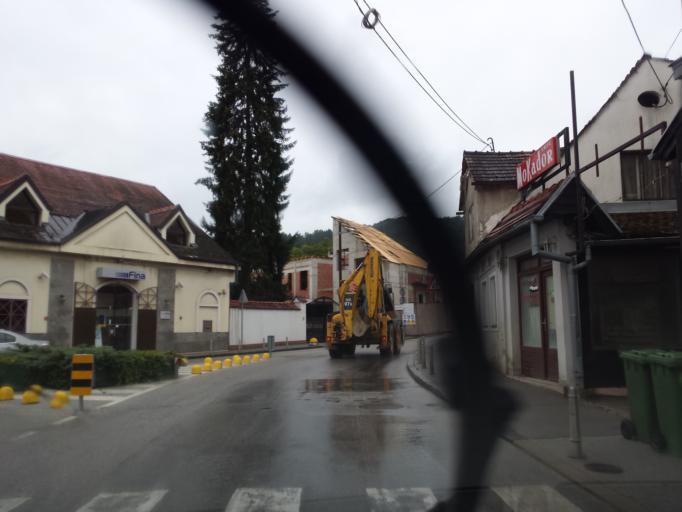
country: HR
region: Zagrebacka
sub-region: Grad Samobor
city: Samobor
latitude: 45.8031
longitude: 15.7092
